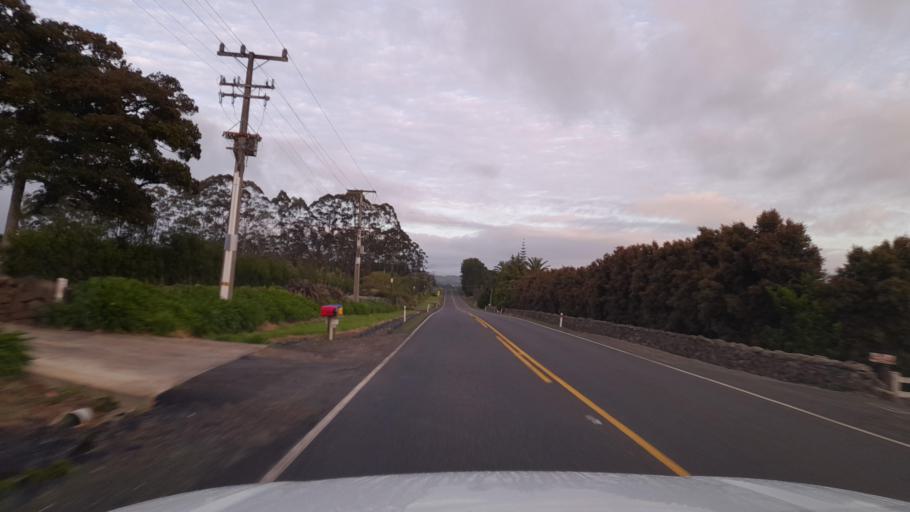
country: NZ
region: Northland
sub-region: Whangarei
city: Maungatapere
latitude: -35.7467
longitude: 174.1583
